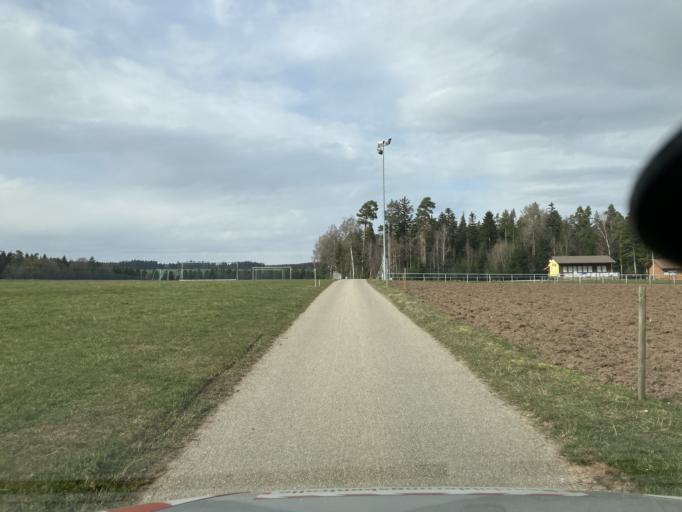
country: DE
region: Baden-Wuerttemberg
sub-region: Karlsruhe Region
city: Neuweiler
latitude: 48.6702
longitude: 8.6363
